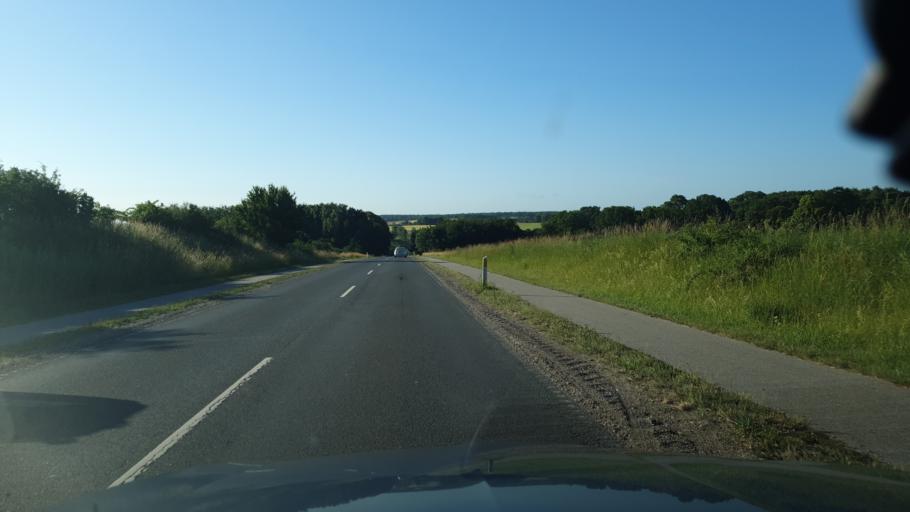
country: DK
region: Zealand
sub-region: Soro Kommune
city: Frederiksberg
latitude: 55.3915
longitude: 11.6417
